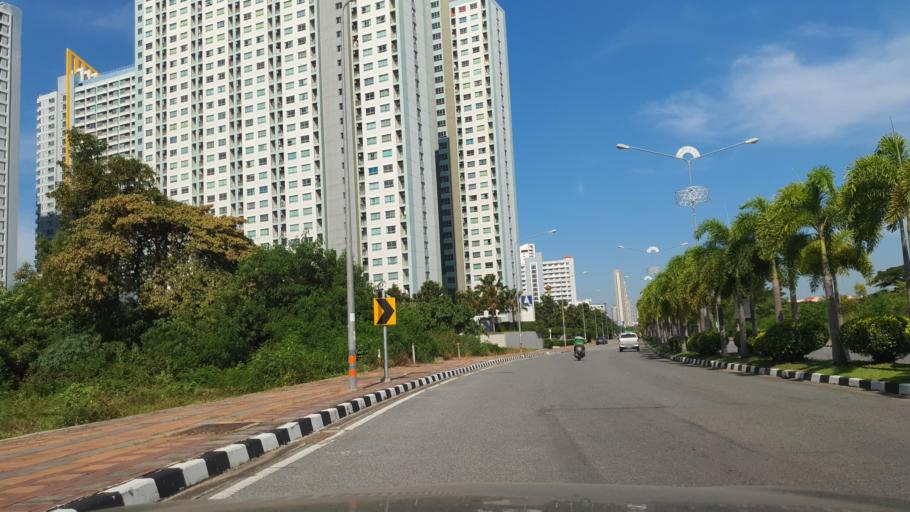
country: TH
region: Chon Buri
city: Phatthaya
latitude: 12.8705
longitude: 100.8946
